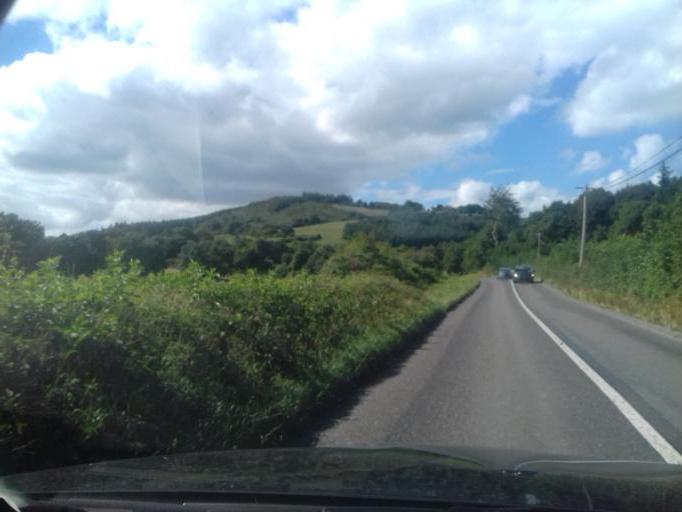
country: IE
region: Munster
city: Carrick-on-Suir
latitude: 52.4008
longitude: -7.4790
